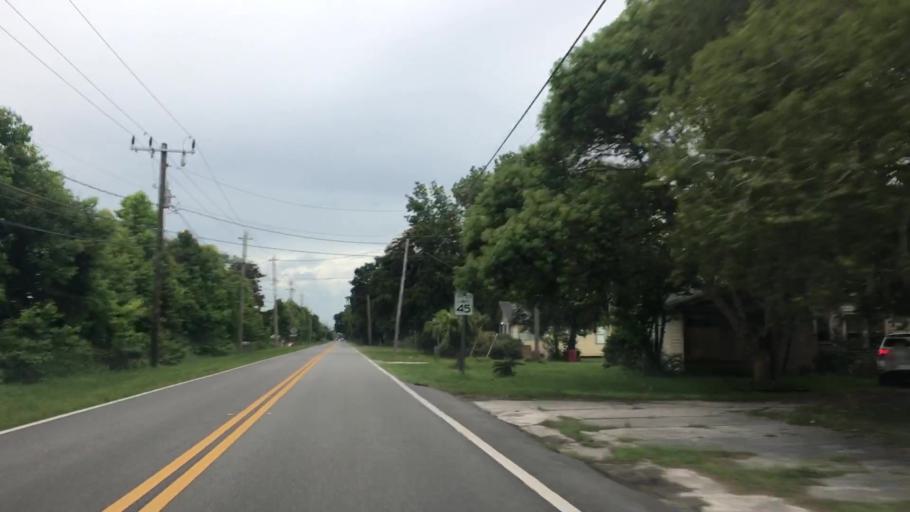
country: US
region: Florida
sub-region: Seminole County
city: Midway
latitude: 28.8014
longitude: -81.2235
